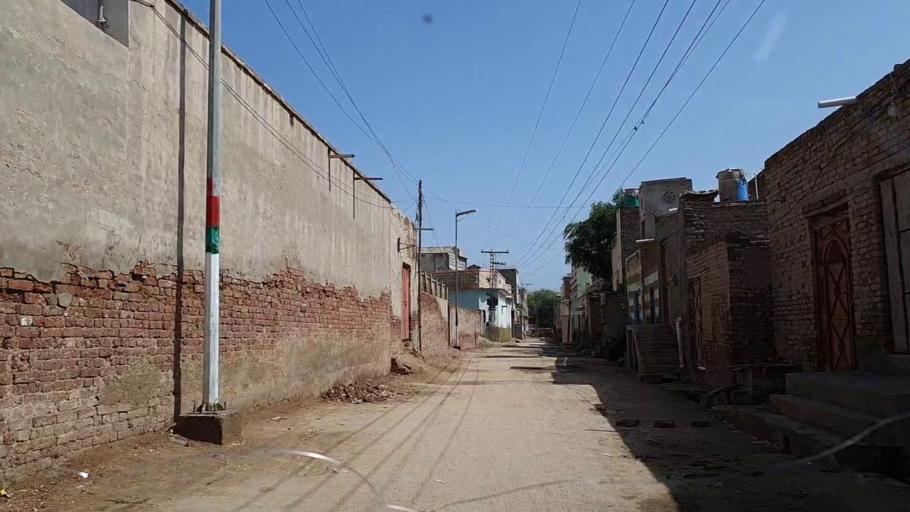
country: PK
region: Sindh
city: Pad Idan
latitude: 26.7739
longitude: 68.2998
